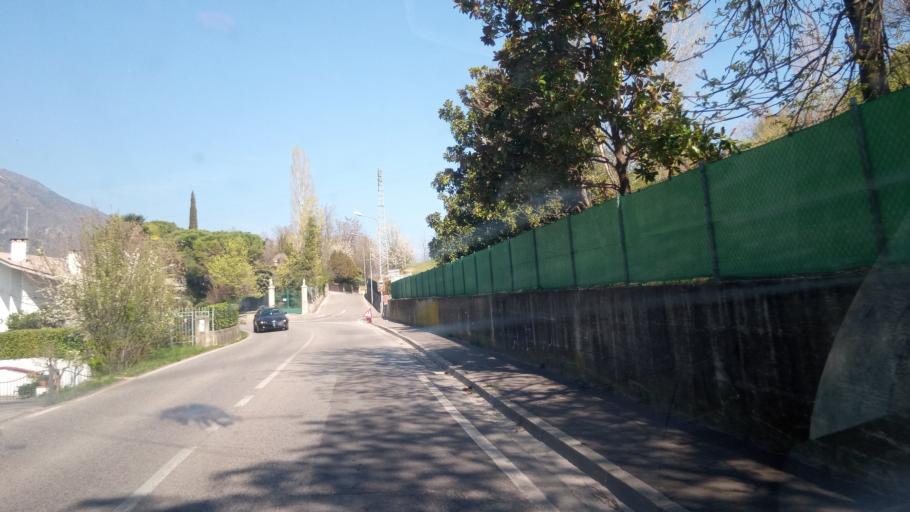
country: IT
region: Veneto
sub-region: Provincia di Treviso
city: Borso del Grappa
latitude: 45.7988
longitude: 11.7624
